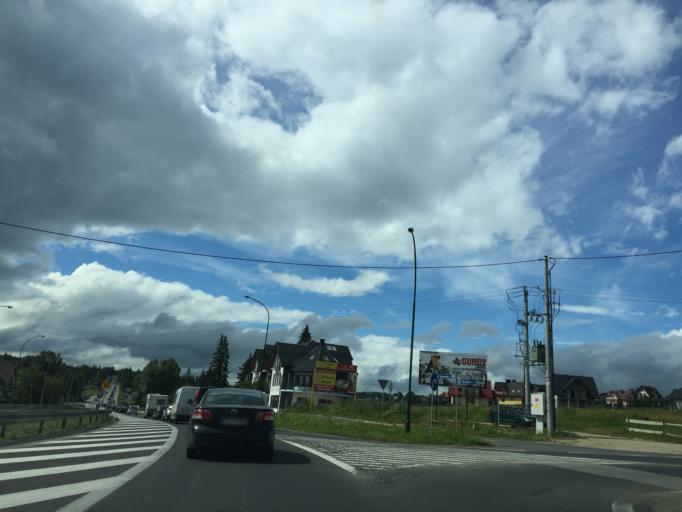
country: PL
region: Lesser Poland Voivodeship
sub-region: Powiat nowotarski
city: Nowy Targ
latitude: 49.4900
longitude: 20.0173
